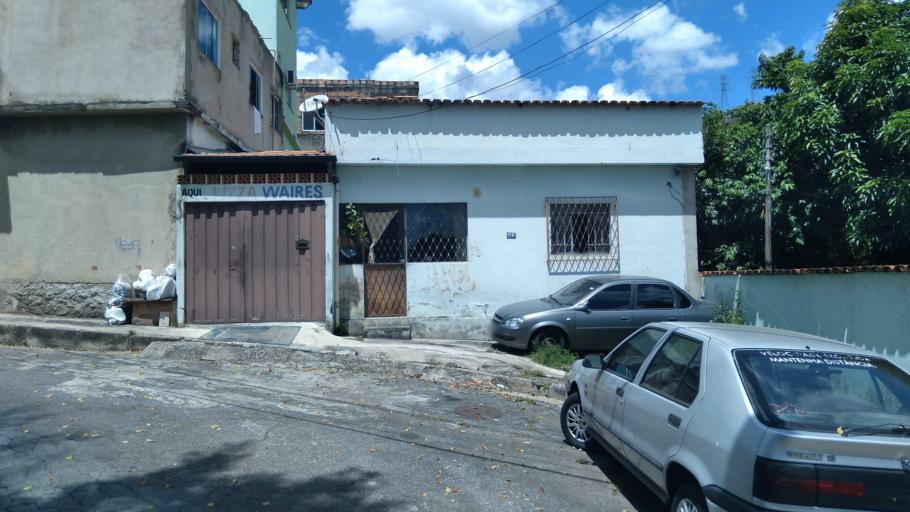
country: BR
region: Minas Gerais
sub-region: Belo Horizonte
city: Belo Horizonte
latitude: -19.8696
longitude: -43.9107
